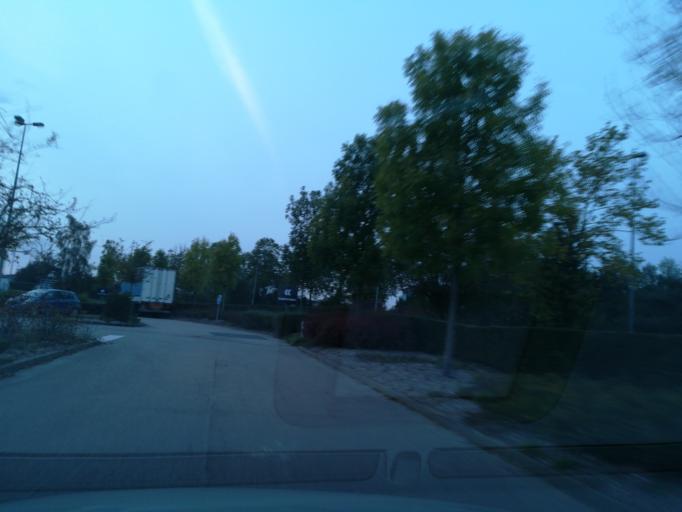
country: FR
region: Haute-Normandie
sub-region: Departement de la Seine-Maritime
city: Isneauville
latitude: 49.4890
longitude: 1.1459
